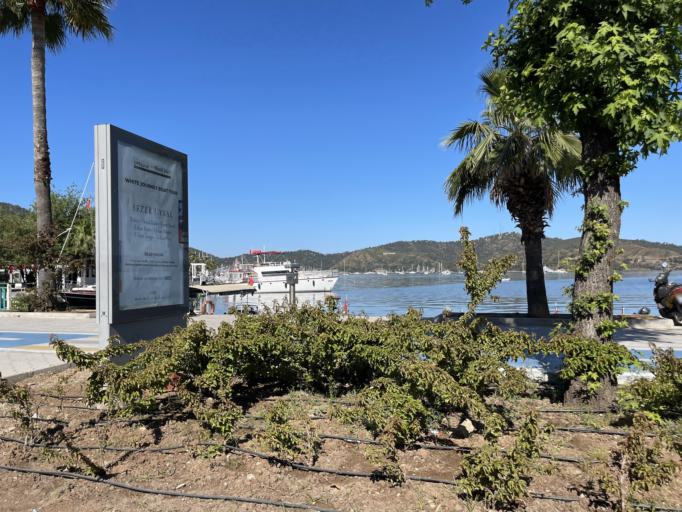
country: TR
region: Mugla
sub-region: Fethiye
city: Fethiye
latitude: 36.6256
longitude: 29.1160
